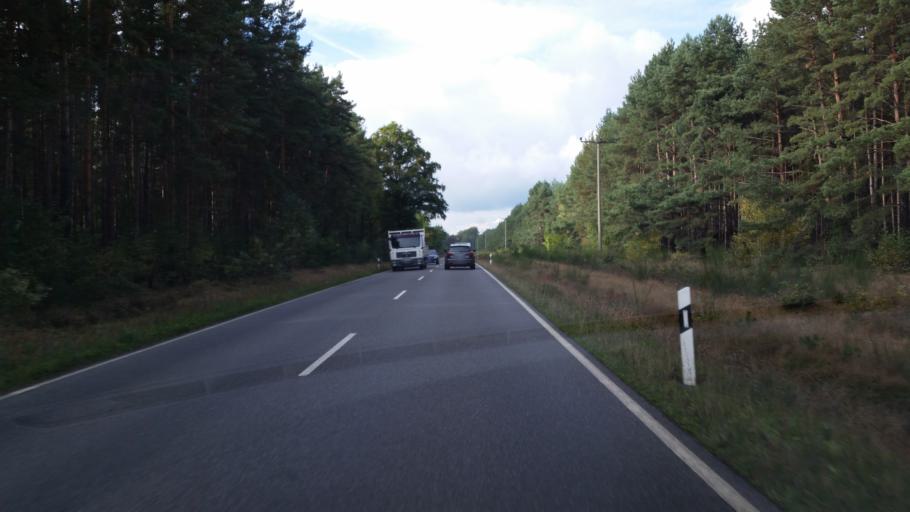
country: DE
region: Brandenburg
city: Guteborn
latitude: 51.4141
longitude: 13.9464
